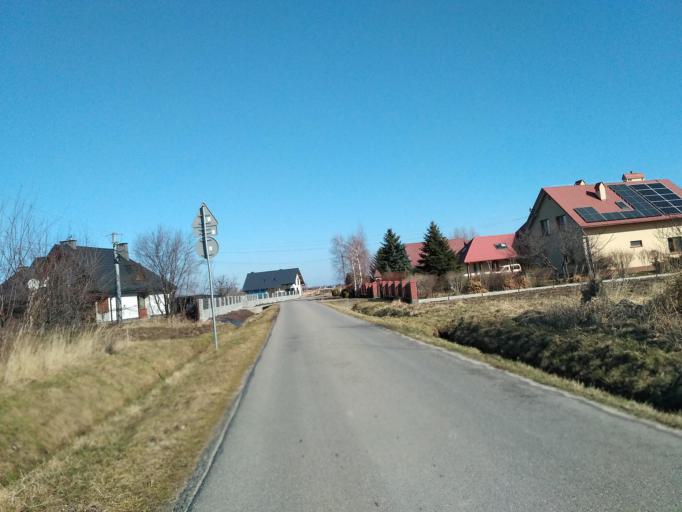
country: PL
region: Subcarpathian Voivodeship
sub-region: Powiat rzeszowski
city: Lutoryz
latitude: 49.9550
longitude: 21.9216
